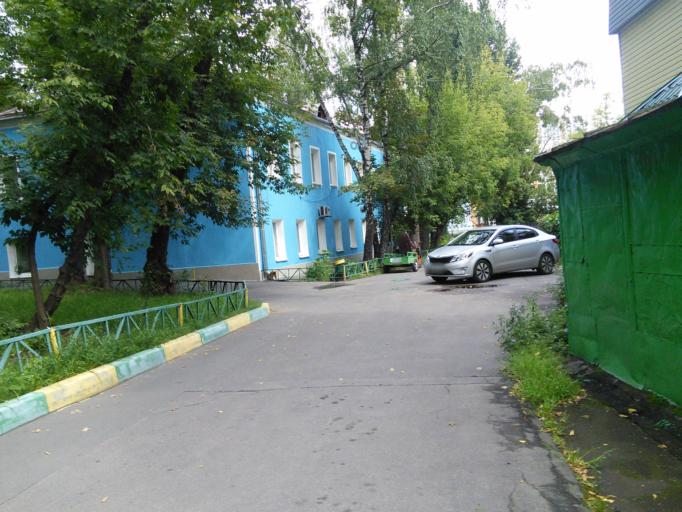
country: RU
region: Moskovskaya
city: Bogorodskoye
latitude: 55.7928
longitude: 37.7265
